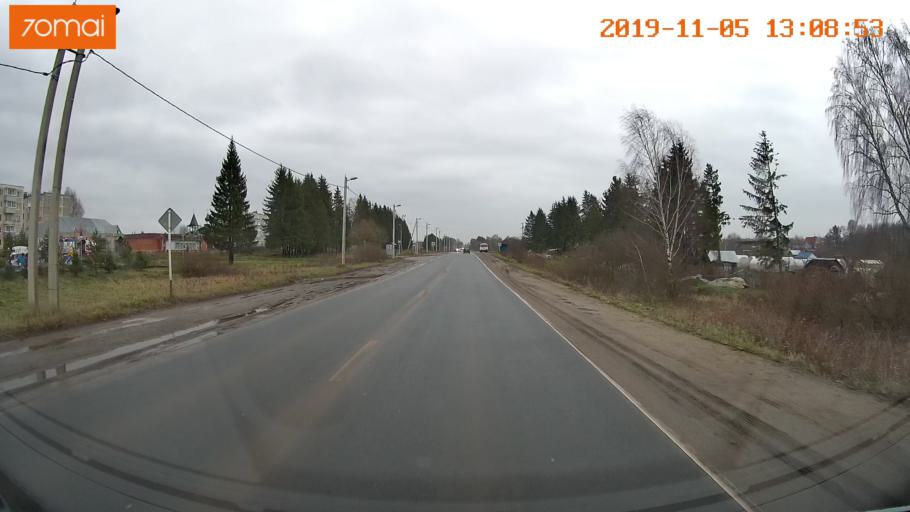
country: RU
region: Ivanovo
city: Kitovo
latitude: 56.8635
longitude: 41.2988
